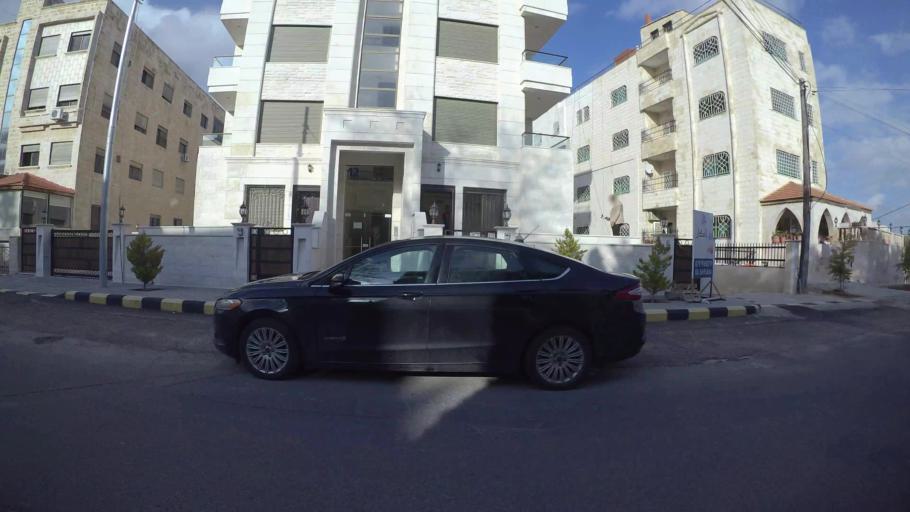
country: JO
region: Amman
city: Al Jubayhah
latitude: 32.0072
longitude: 35.8607
